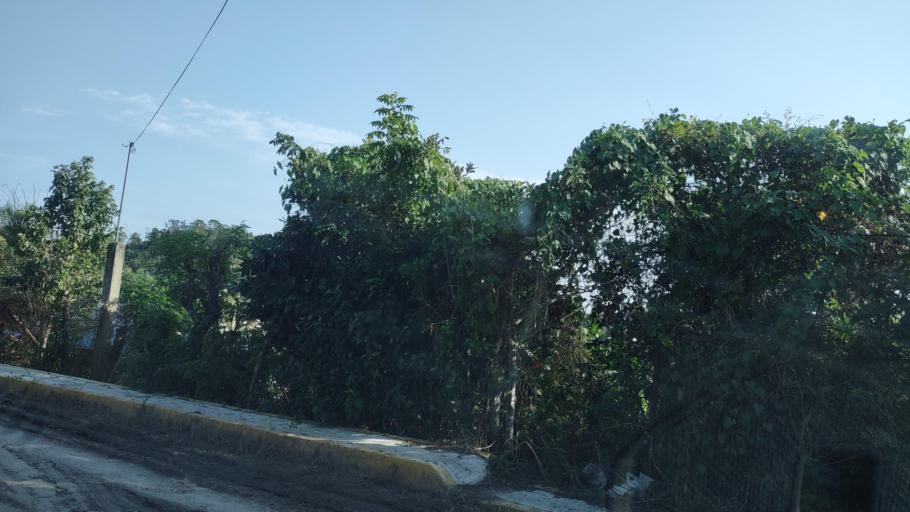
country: MX
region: Veracruz
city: Papantla de Olarte
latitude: 20.4606
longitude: -97.3648
